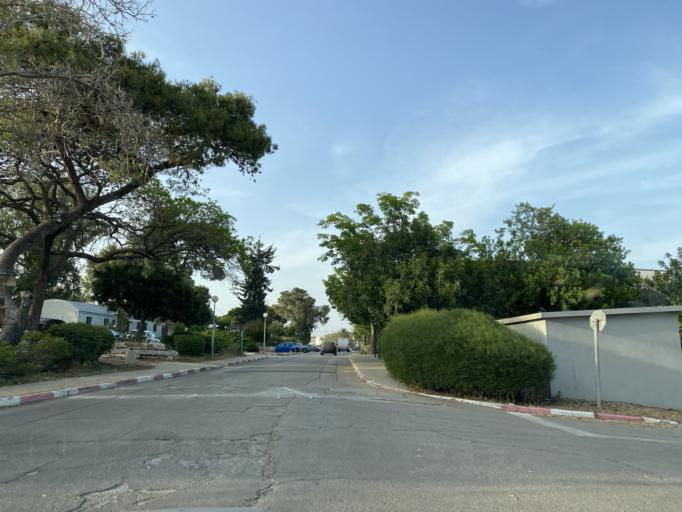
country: IL
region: Tel Aviv
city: Herzliyya
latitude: 32.1578
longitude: 34.8320
